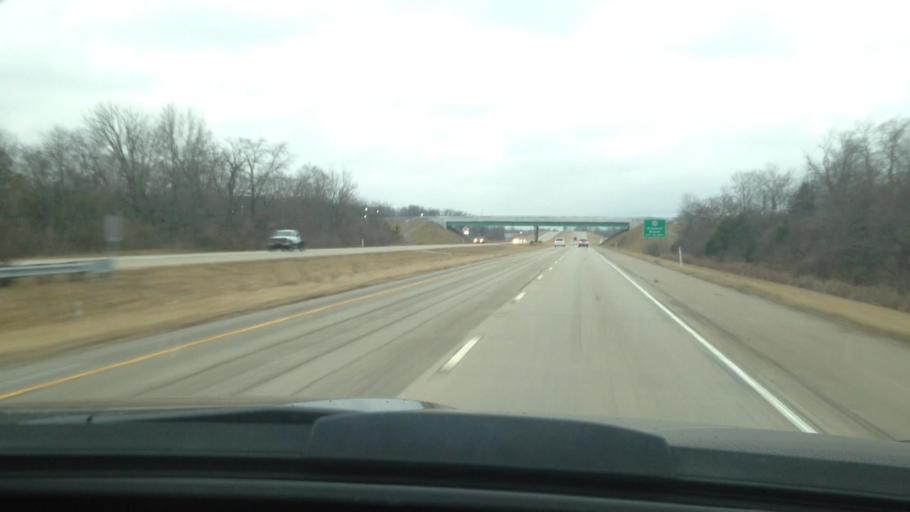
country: US
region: Indiana
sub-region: Delaware County
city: Muncie
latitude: 40.1719
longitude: -85.3422
